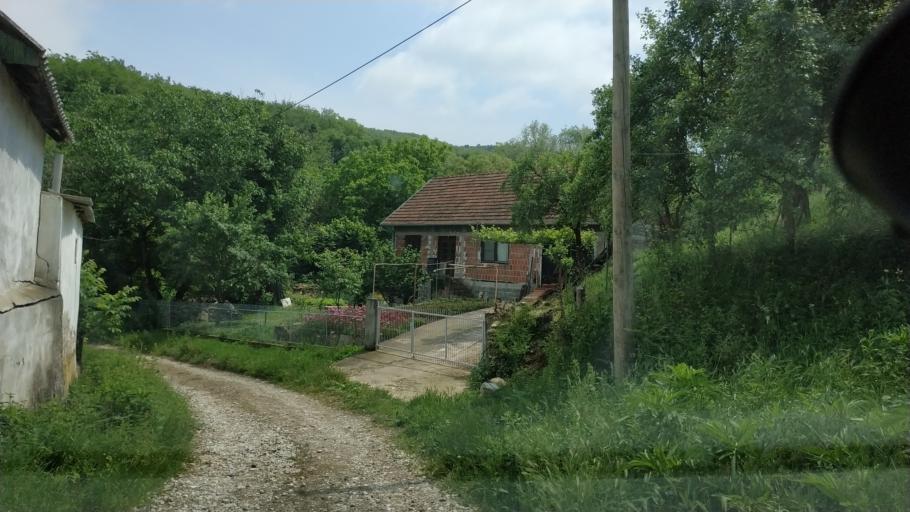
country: RS
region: Central Serbia
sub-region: Nisavski Okrug
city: Aleksinac
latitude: 43.4128
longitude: 21.7173
